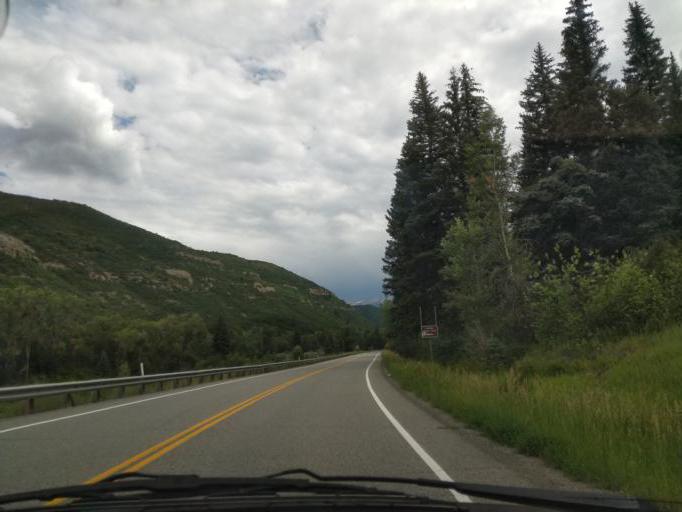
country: US
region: Colorado
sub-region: Delta County
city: Paonia
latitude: 38.9919
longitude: -107.3514
